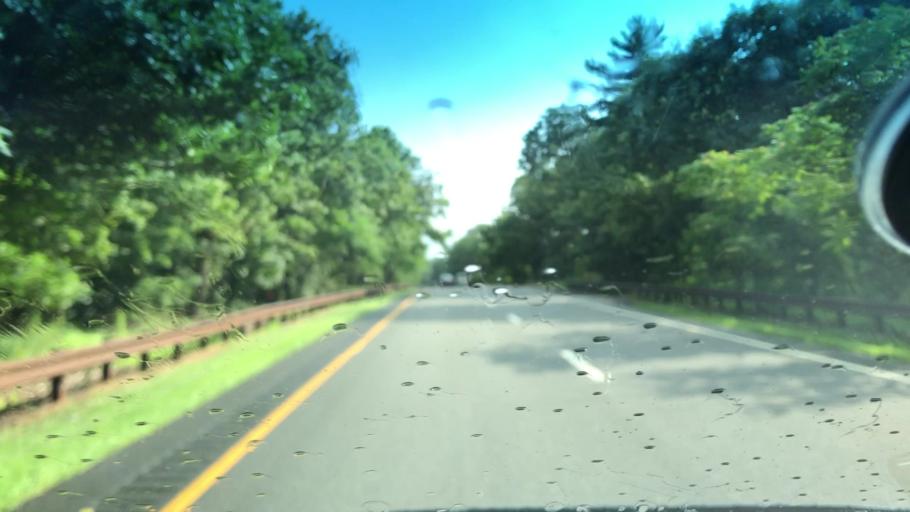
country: US
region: New Jersey
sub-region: Bergen County
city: Englewood Cliffs
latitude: 40.8978
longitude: -73.9390
